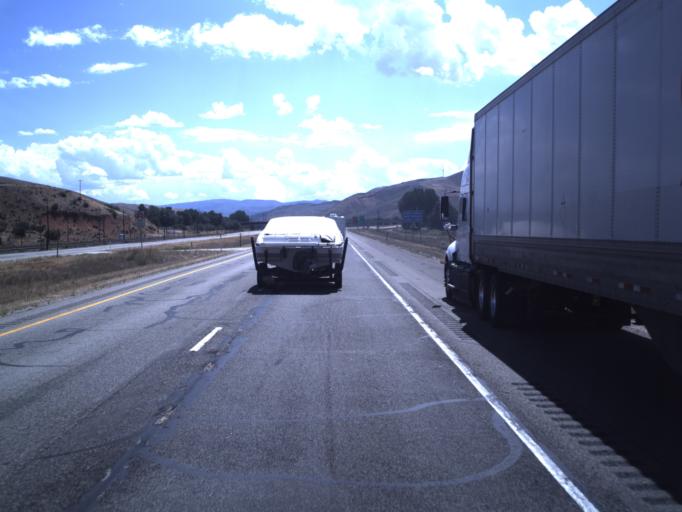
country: US
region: Utah
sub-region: Summit County
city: Coalville
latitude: 41.0231
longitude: -111.4957
